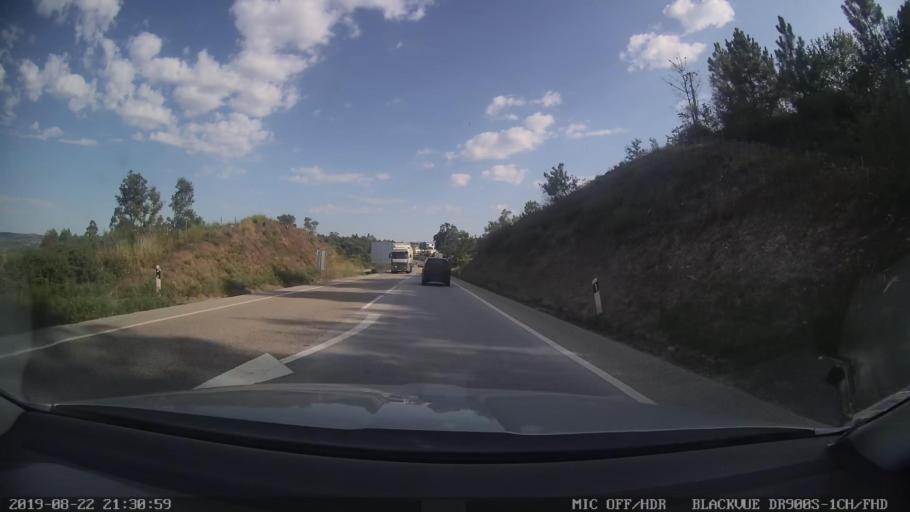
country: PT
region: Leiria
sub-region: Pedrogao Grande
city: Pedrogao Grande
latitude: 39.9151
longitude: -8.1537
